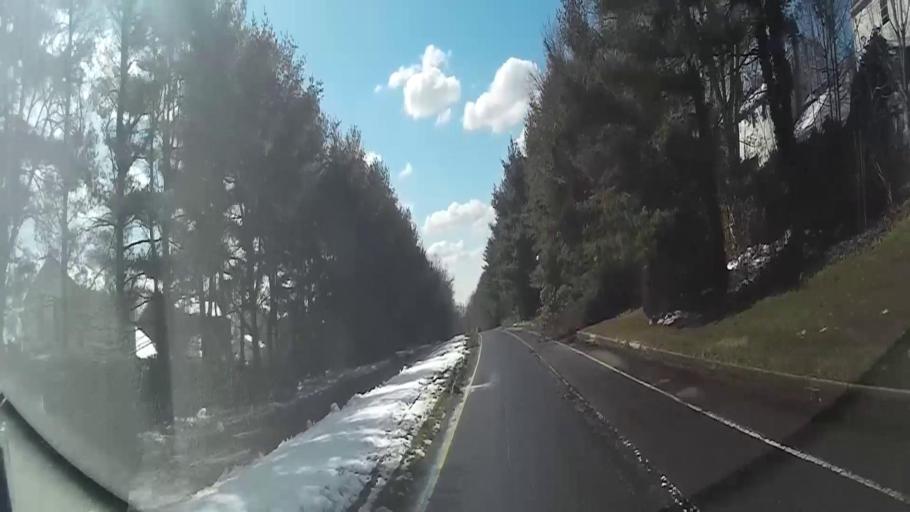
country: US
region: New Jersey
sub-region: Burlington County
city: Marlton
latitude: 39.8748
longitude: -74.9124
